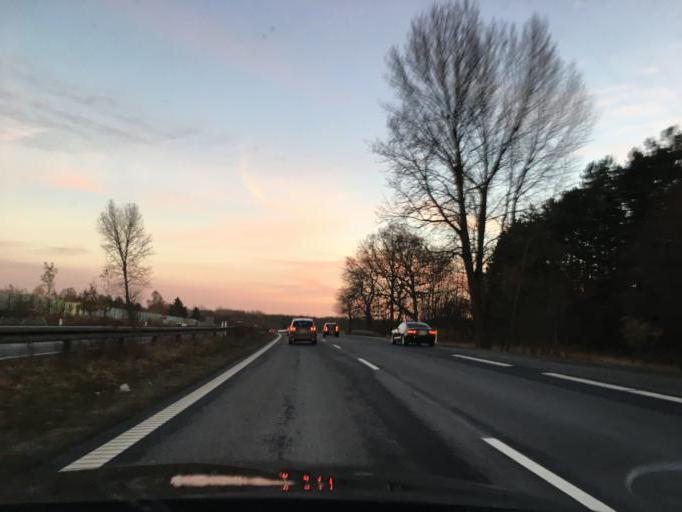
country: DK
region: Capital Region
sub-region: Horsholm Kommune
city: Horsholm
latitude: 55.8649
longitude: 12.4857
